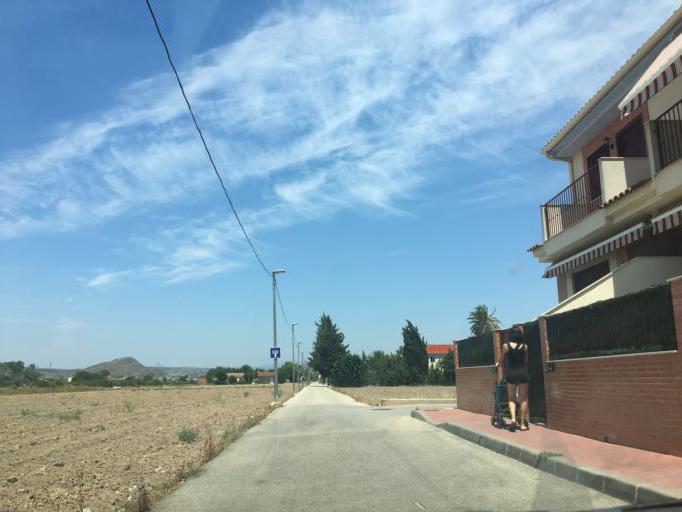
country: ES
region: Murcia
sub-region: Murcia
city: Santomera
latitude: 38.0168
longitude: -1.0550
